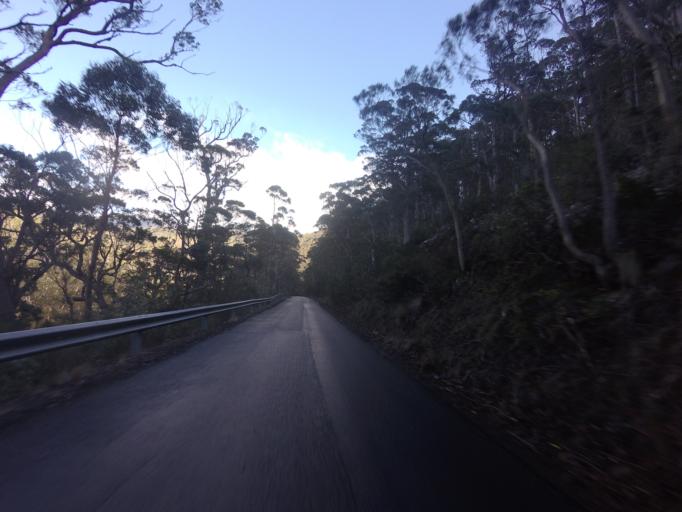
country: AU
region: Tasmania
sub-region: Glenorchy
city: Berriedale
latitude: -42.8205
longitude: 147.1873
